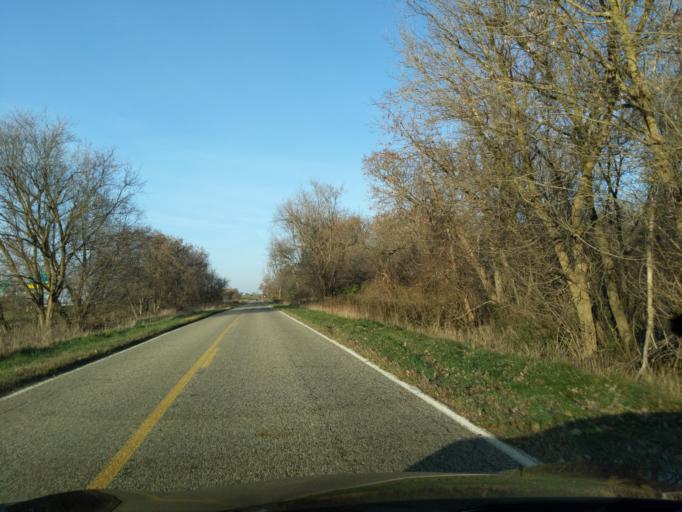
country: US
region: Michigan
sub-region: Ingham County
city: East Lansing
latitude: 42.7947
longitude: -84.5117
